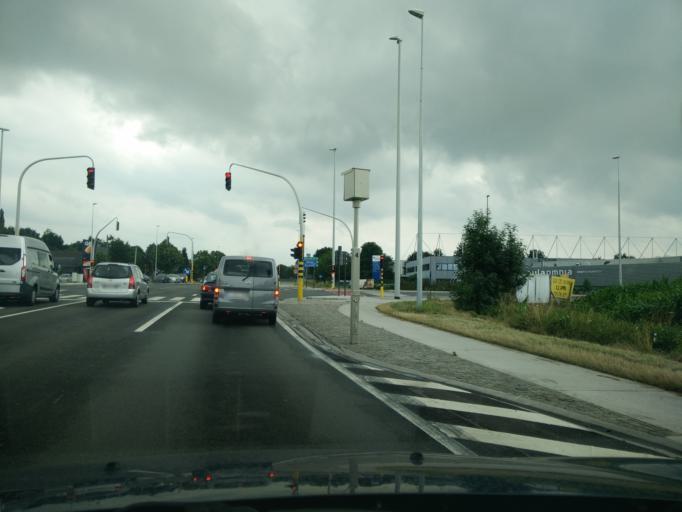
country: BE
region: Flanders
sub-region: Provincie Oost-Vlaanderen
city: Gavere
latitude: 50.9309
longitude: 3.6280
